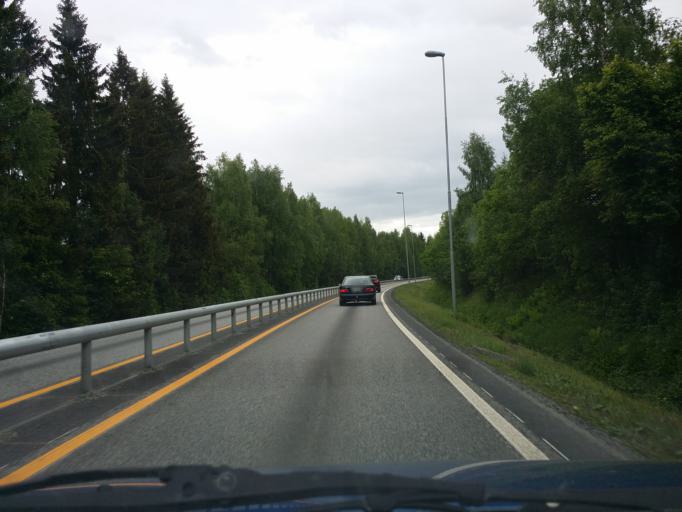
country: NO
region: Hedmark
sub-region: Ringsaker
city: Moelv
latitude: 60.9635
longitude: 10.6187
